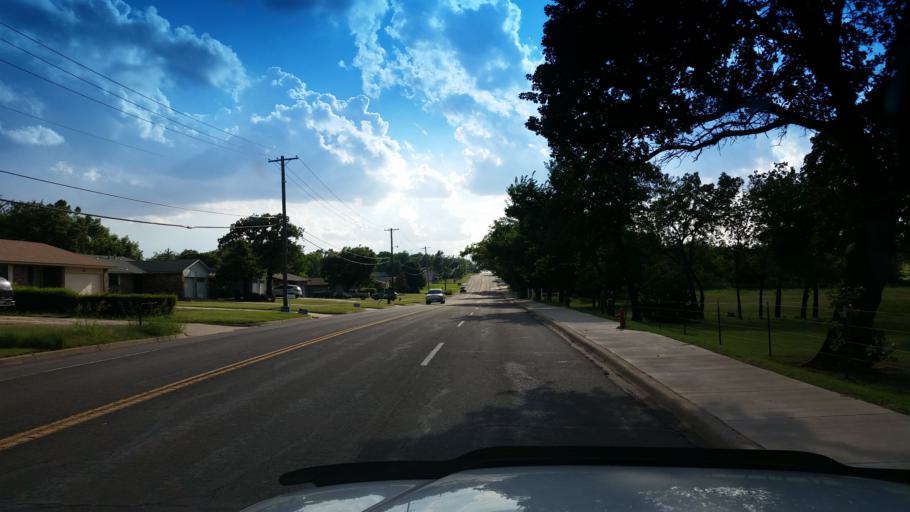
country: US
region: Oklahoma
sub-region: Oklahoma County
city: Nichols Hills
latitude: 35.5369
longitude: -97.5037
